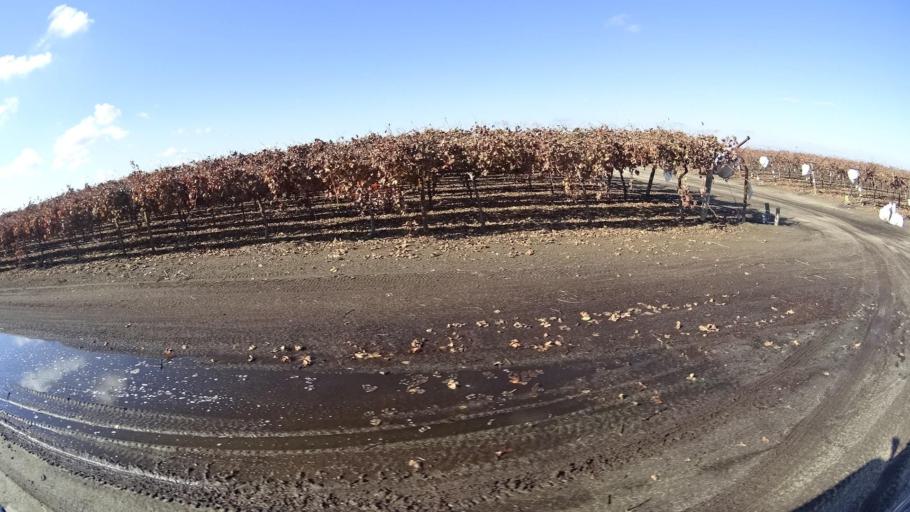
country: US
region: California
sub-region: Kern County
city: McFarland
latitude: 35.7068
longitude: -119.2586
